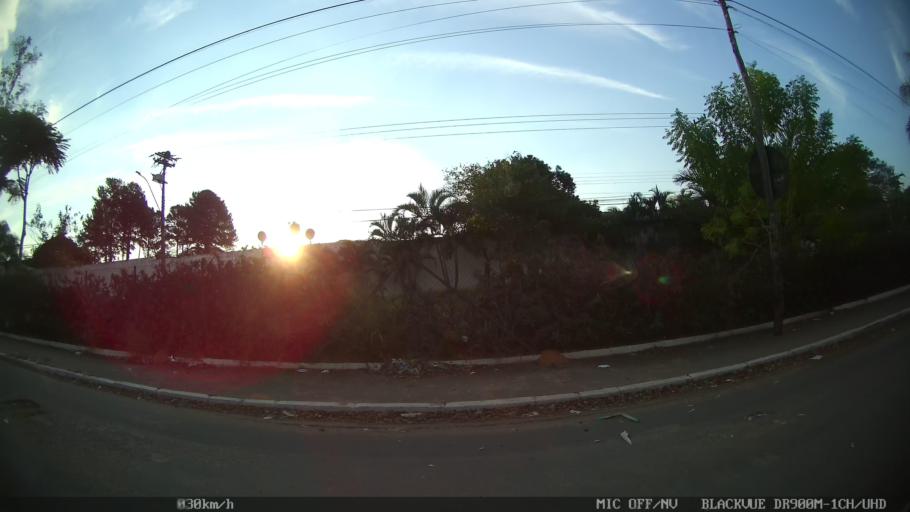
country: BR
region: Sao Paulo
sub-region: Hortolandia
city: Hortolandia
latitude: -22.8823
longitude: -47.1559
